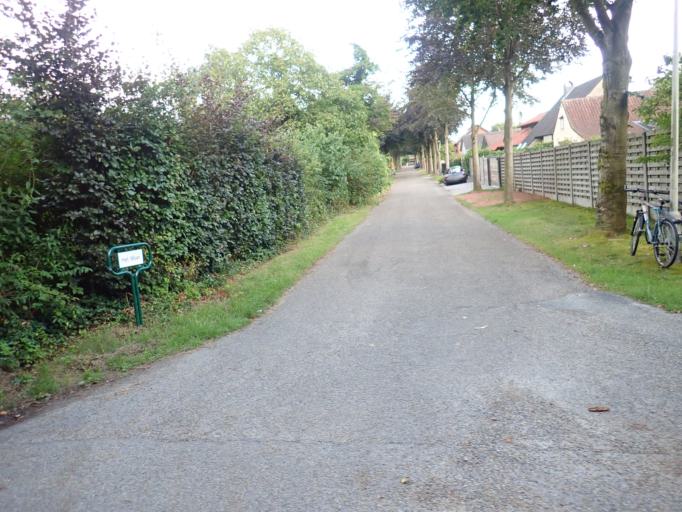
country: BE
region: Flanders
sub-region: Provincie Antwerpen
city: Zoersel
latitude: 51.2640
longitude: 4.6648
